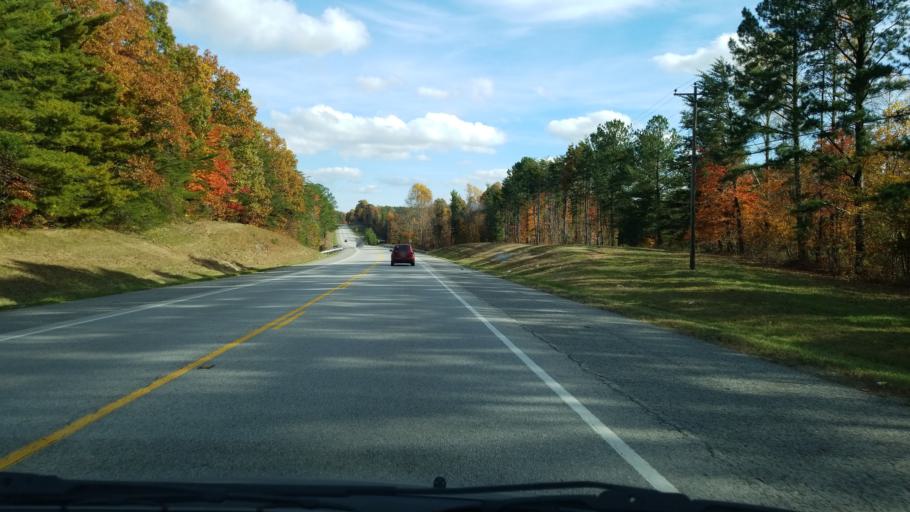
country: US
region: Tennessee
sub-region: Sequatchie County
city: Dunlap
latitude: 35.4433
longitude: -85.4323
